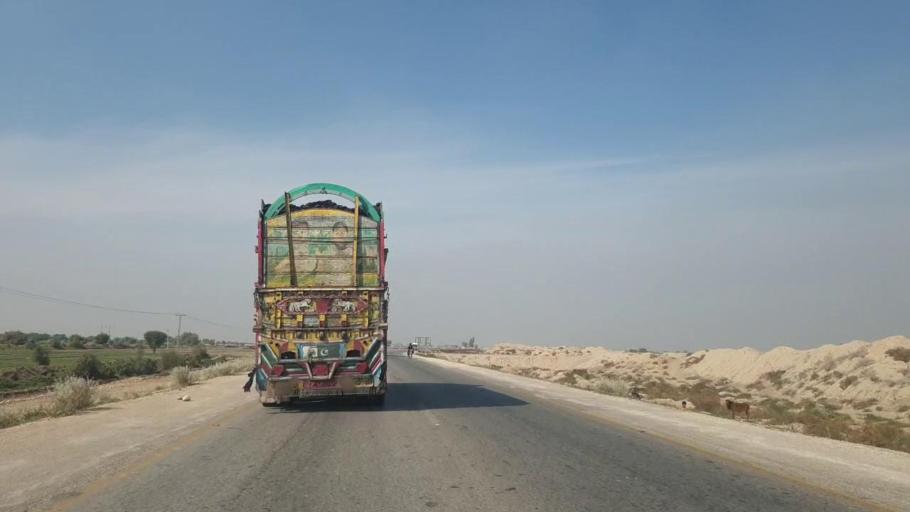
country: PK
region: Sindh
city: Sann
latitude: 25.9537
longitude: 68.1953
